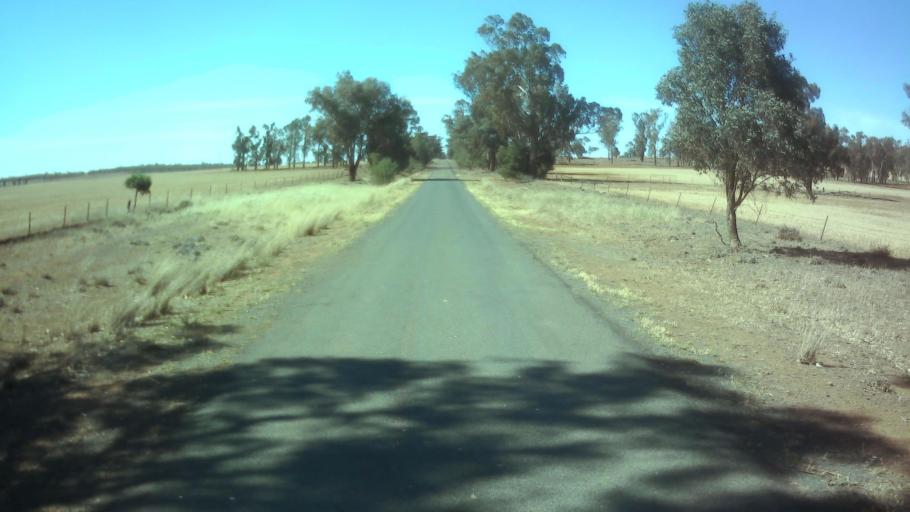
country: AU
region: New South Wales
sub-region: Forbes
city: Forbes
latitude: -33.7344
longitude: 147.7422
